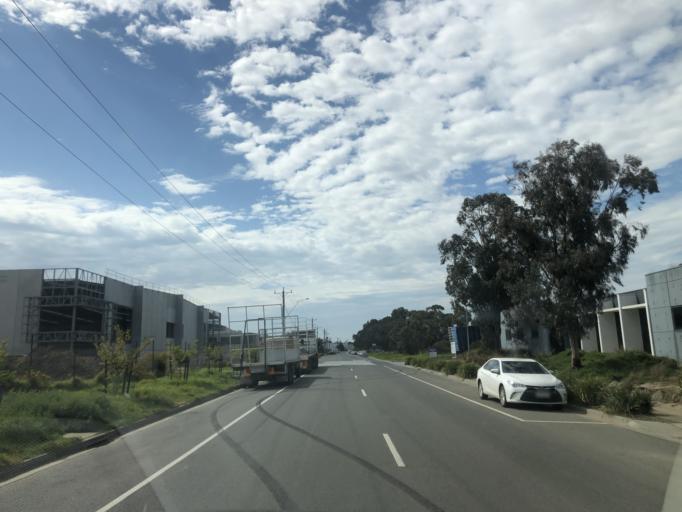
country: AU
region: Victoria
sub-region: Casey
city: Hampton Park
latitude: -38.0381
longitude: 145.2281
